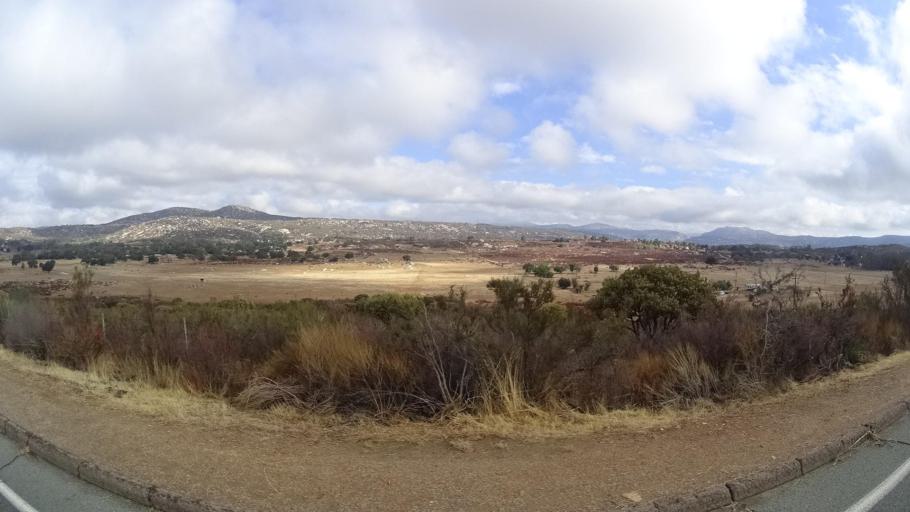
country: MX
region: Baja California
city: Tecate
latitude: 32.6151
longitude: -116.6056
